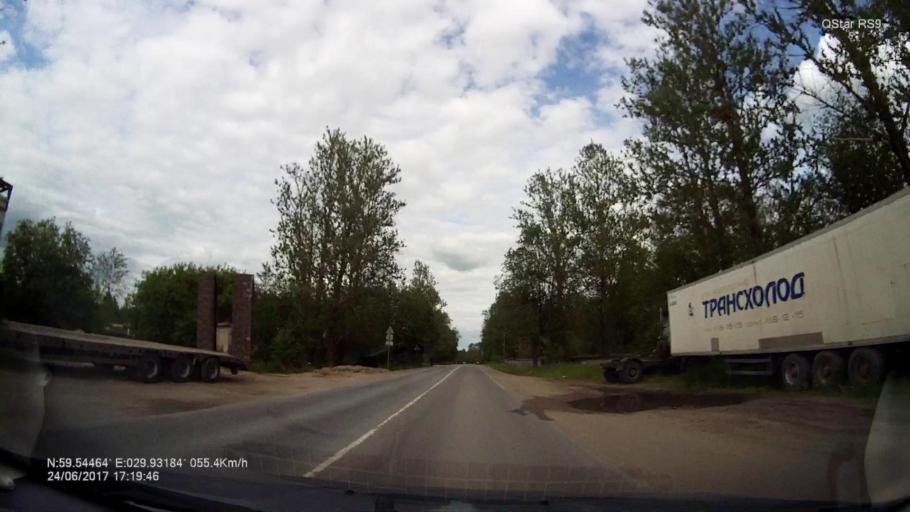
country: RU
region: Leningrad
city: Voyskovitsy
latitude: 59.5447
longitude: 29.9322
